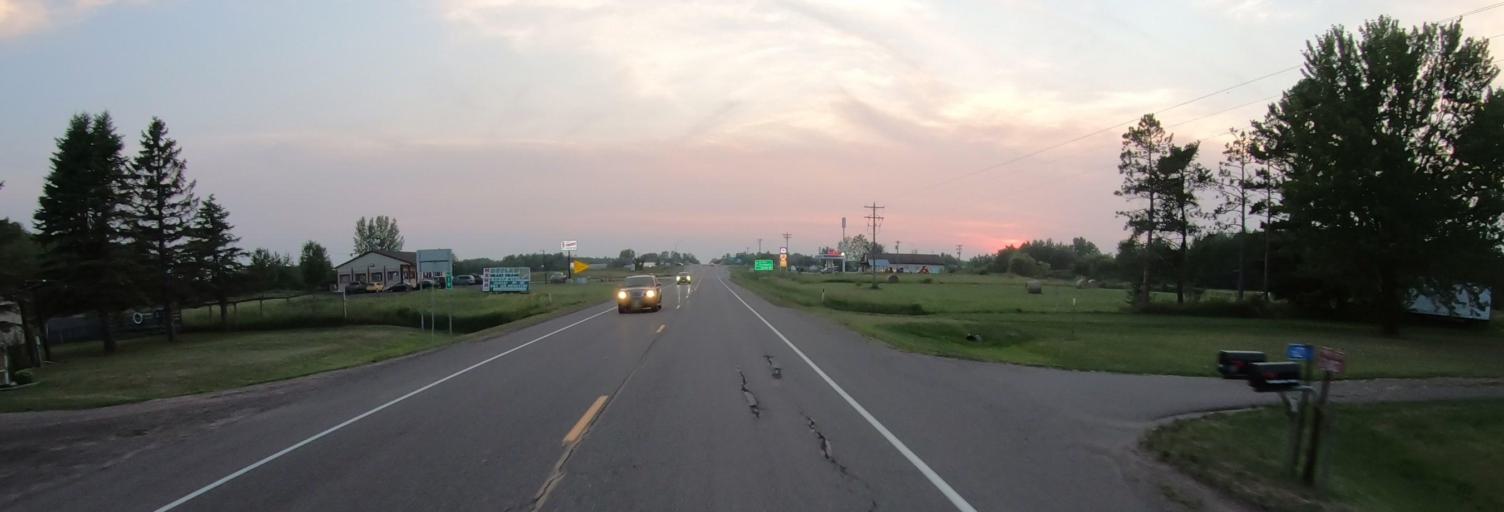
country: US
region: Minnesota
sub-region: Pine County
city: Rock Creek
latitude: 45.7667
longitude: -92.9841
